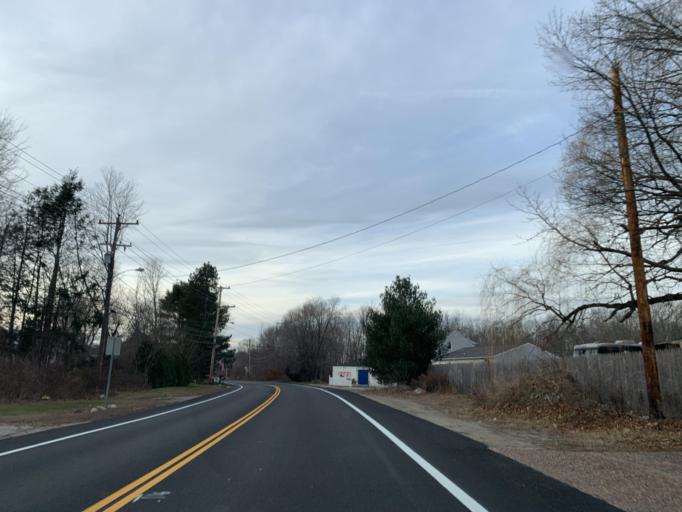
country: US
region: Rhode Island
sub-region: Providence County
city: Greenville
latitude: 41.8548
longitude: -71.5218
